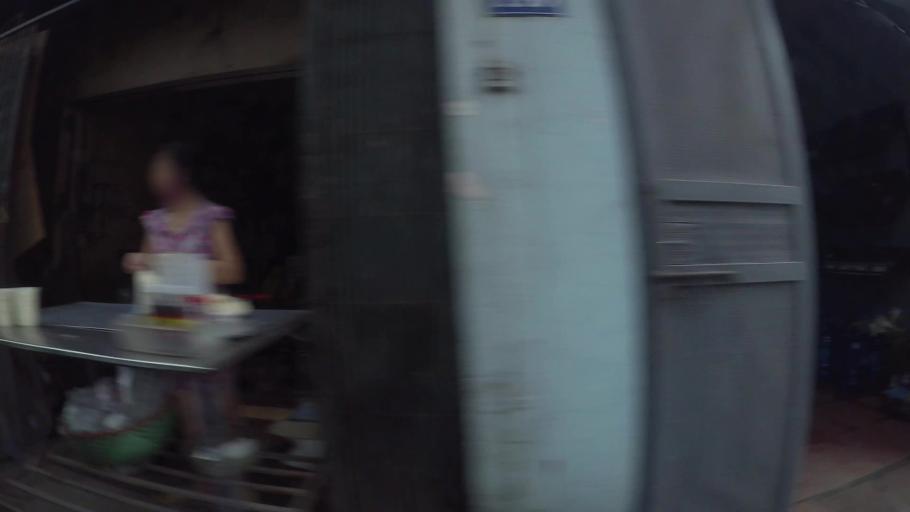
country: VN
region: Ha Noi
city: Hai BaTrung
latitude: 20.9887
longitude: 105.8885
